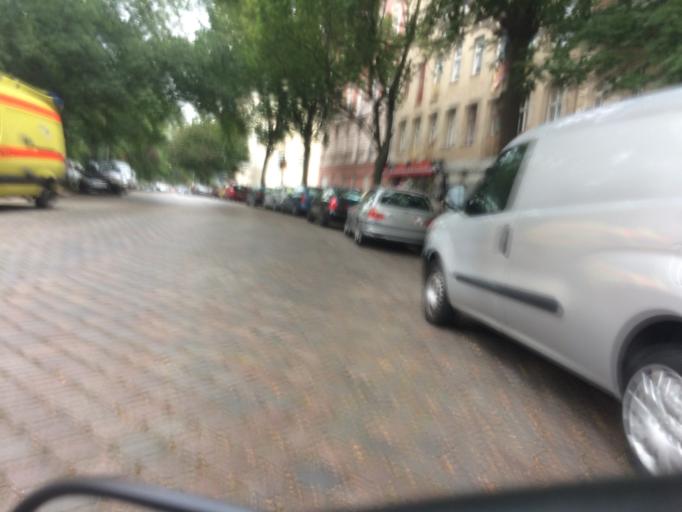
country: DE
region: Berlin
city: Gesundbrunnen
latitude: 52.5611
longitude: 13.3810
